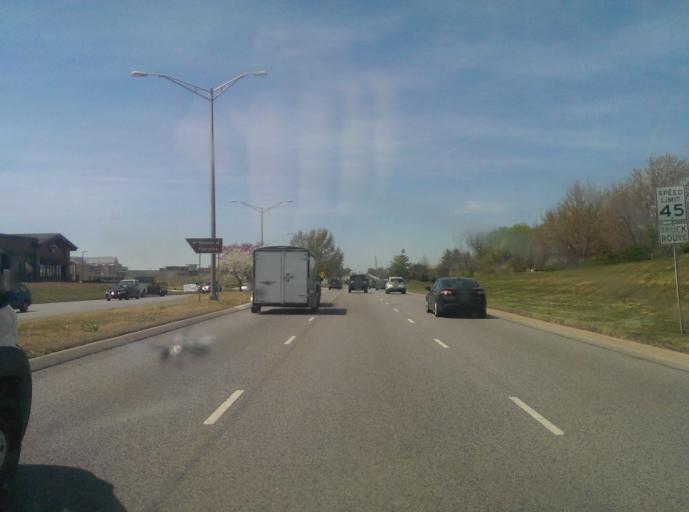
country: US
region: Kansas
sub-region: Johnson County
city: Leawood
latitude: 38.8838
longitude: -94.6503
